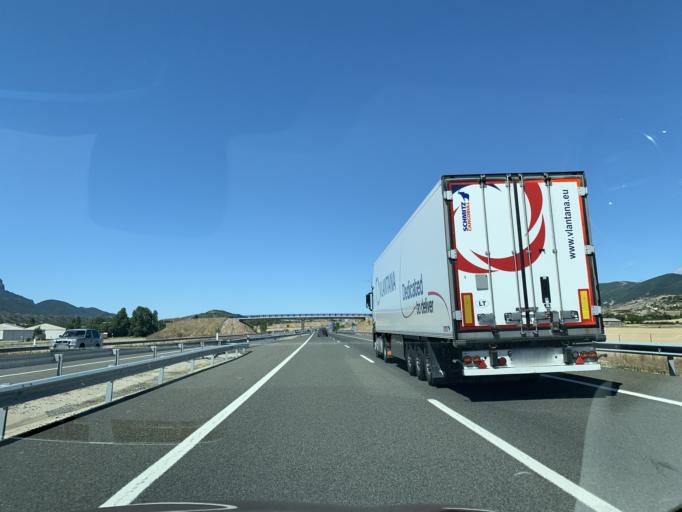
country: ES
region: Aragon
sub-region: Provincia de Huesca
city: Sabinanigo
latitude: 42.5457
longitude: -0.4120
